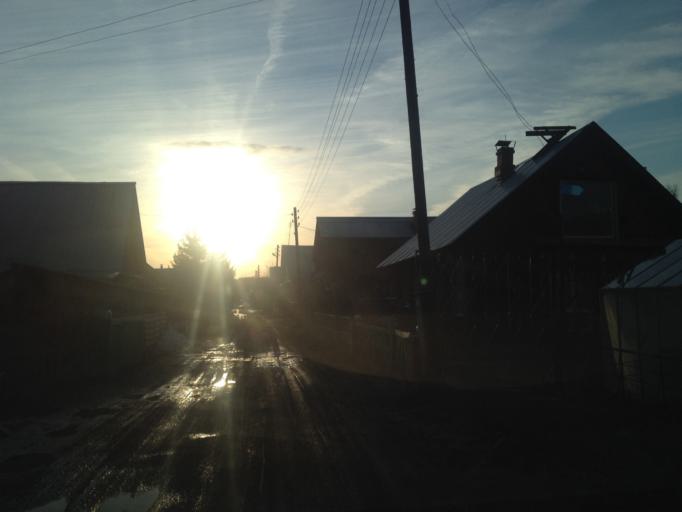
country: RU
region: Sverdlovsk
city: Shirokaya Rechka
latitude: 56.8094
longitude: 60.4309
